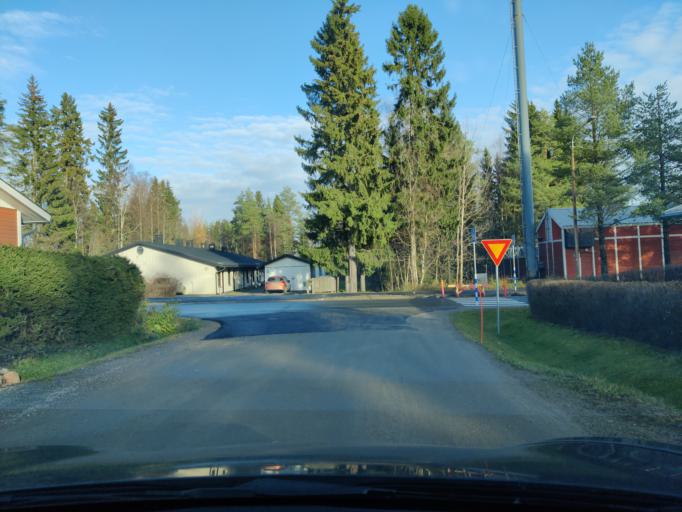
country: FI
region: Northern Savo
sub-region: Ylae-Savo
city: Kiuruvesi
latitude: 63.6448
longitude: 26.6295
